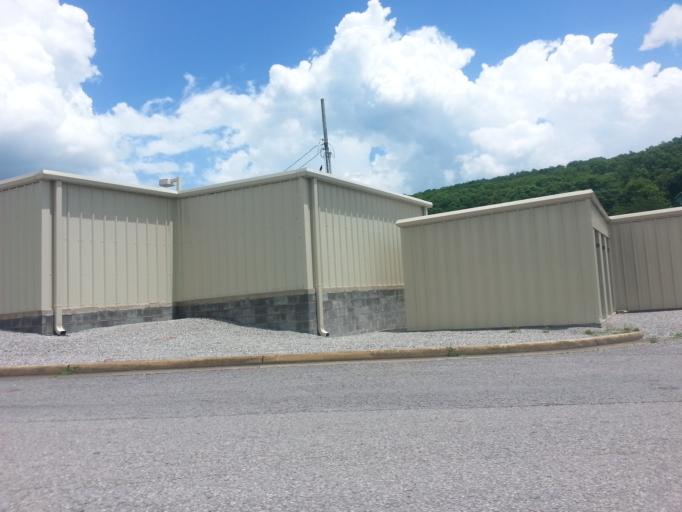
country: US
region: Tennessee
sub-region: Claiborne County
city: Harrogate
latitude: 36.5952
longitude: -83.6626
